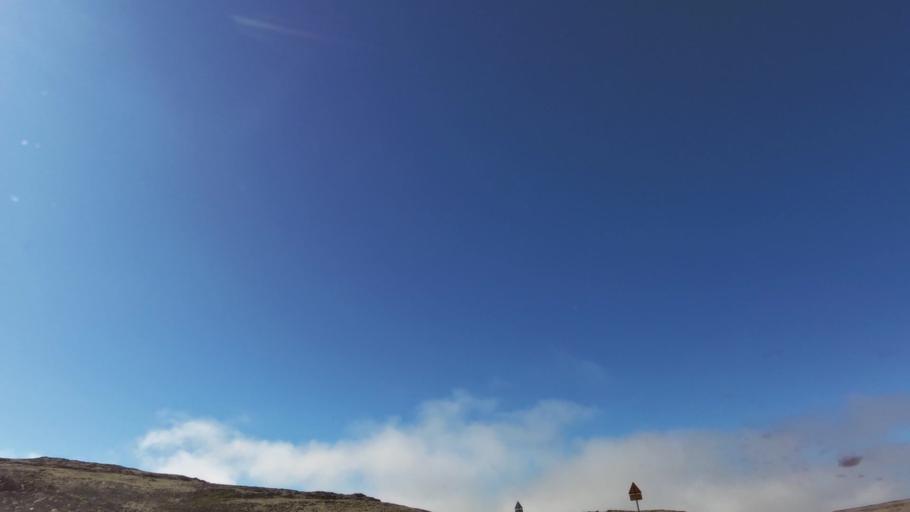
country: IS
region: West
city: Olafsvik
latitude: 65.5515
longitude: -24.2176
